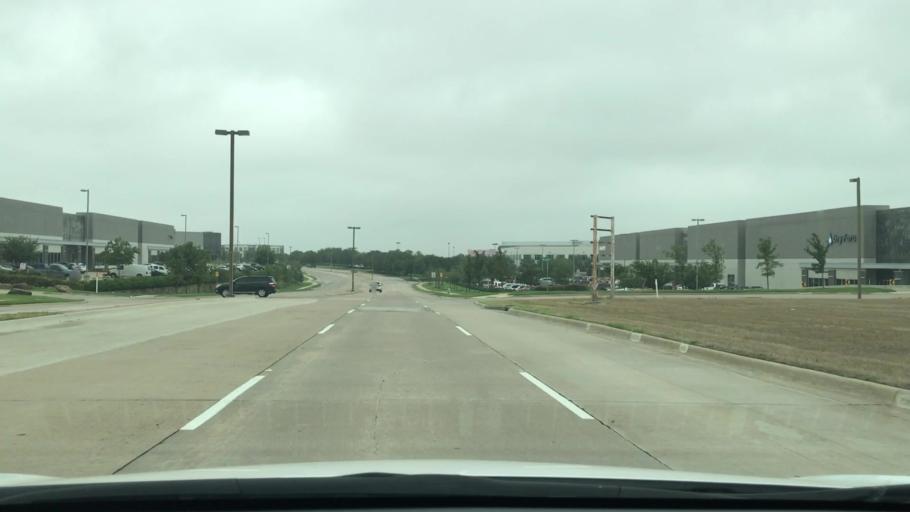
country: US
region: Texas
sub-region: Dallas County
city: Coppell
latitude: 32.9160
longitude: -96.9988
